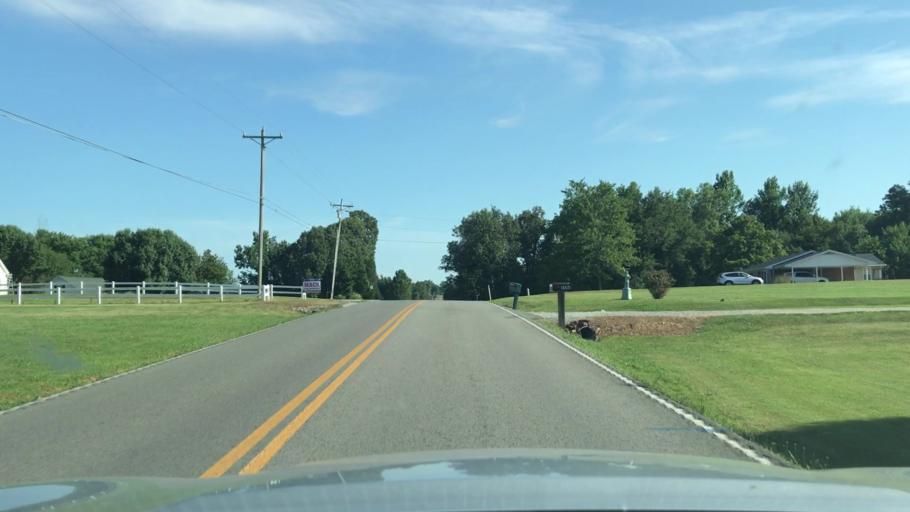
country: US
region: Kentucky
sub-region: Muhlenberg County
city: Greenville
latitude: 37.1473
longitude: -87.1412
